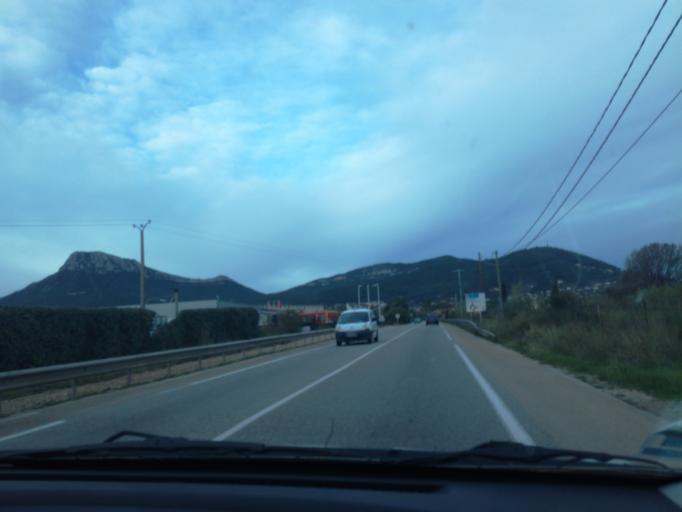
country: FR
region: Provence-Alpes-Cote d'Azur
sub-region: Departement du Var
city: La Crau
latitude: 43.1601
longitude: 6.0624
